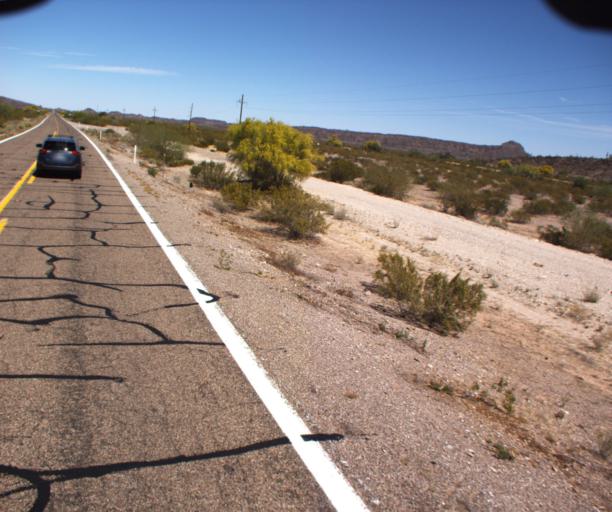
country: US
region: Arizona
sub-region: Pima County
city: Ajo
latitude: 32.5015
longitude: -112.8811
